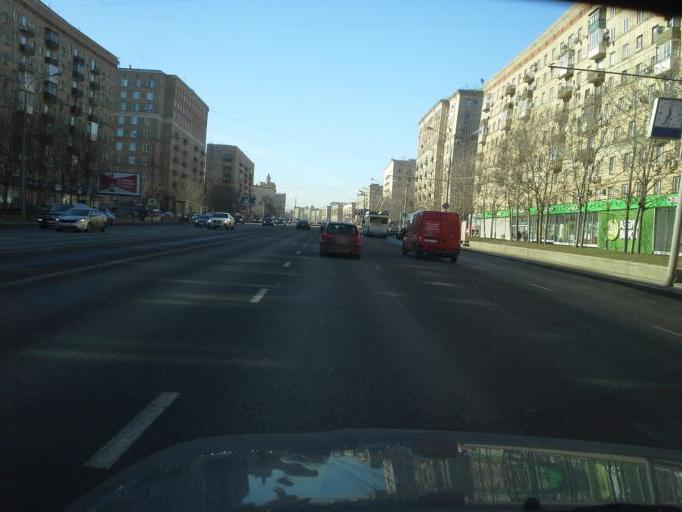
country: RU
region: Moskovskaya
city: Dorogomilovo
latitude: 55.7492
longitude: 37.5619
